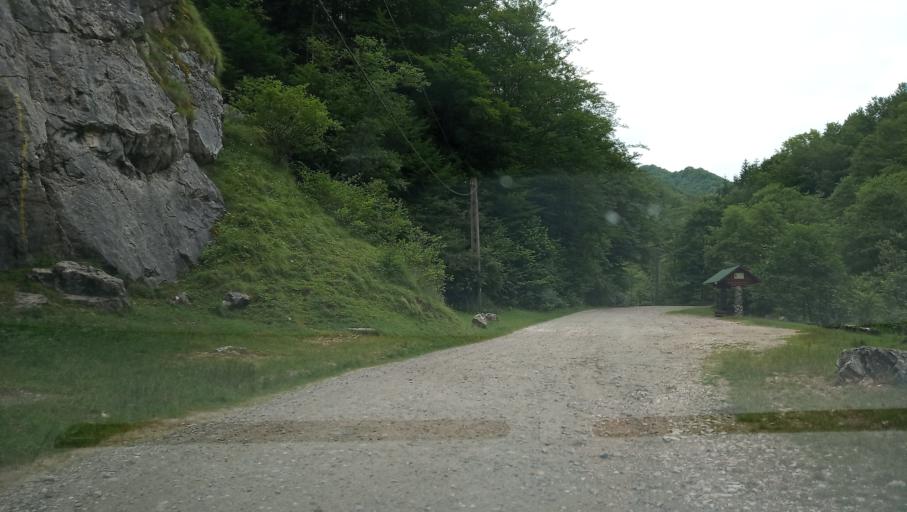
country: RO
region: Hunedoara
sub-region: Oras Petrila
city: Petrila
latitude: 45.4739
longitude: 23.4169
